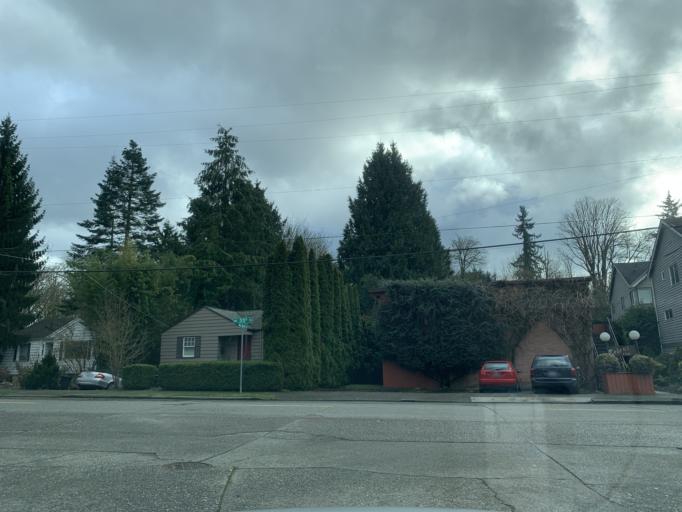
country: US
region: Washington
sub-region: King County
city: Yarrow Point
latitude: 47.6694
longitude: -122.2780
